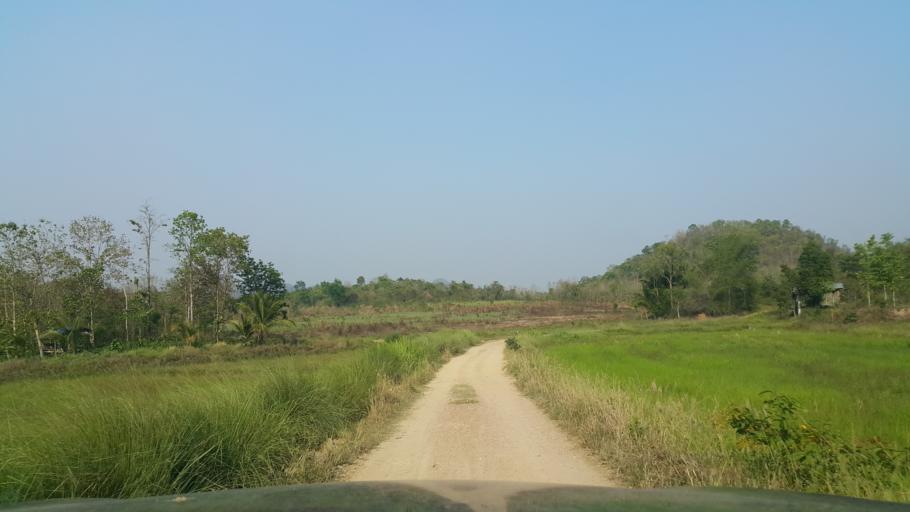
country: TH
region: Sukhothai
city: Thung Saliam
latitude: 17.3339
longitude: 99.4647
